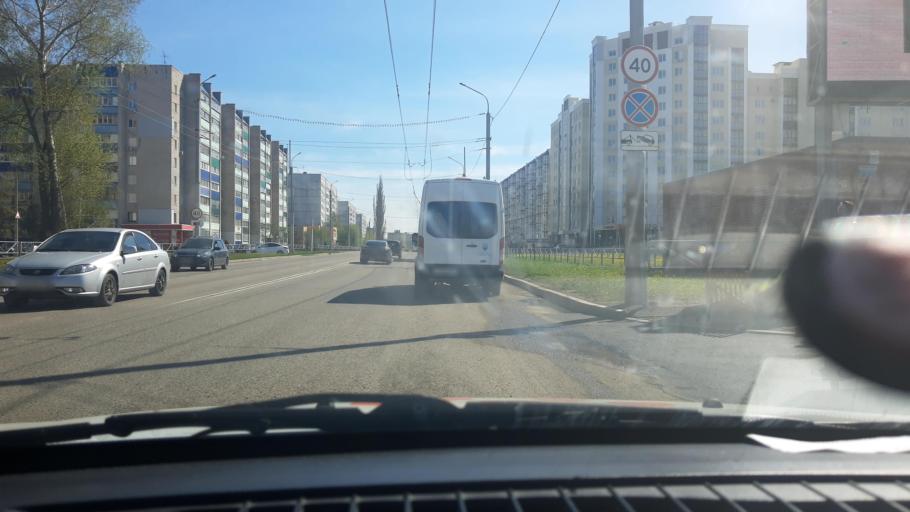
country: RU
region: Bashkortostan
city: Sterlitamak
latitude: 53.6301
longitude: 55.9037
